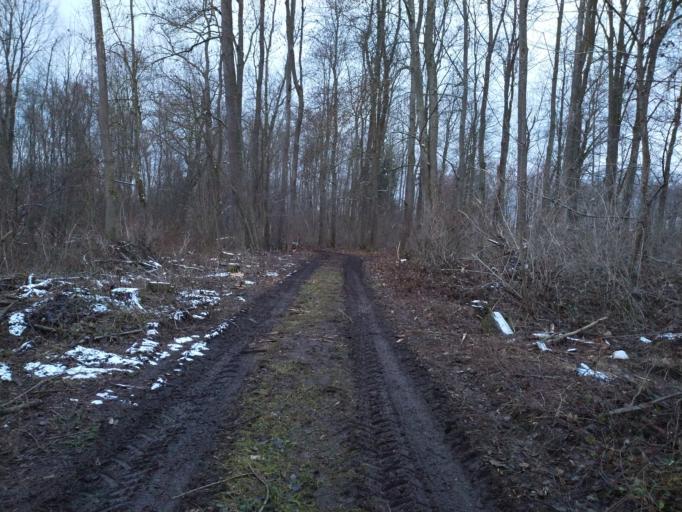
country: DE
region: Bavaria
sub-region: Swabia
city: Rettenbach
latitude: 48.4796
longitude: 10.3156
